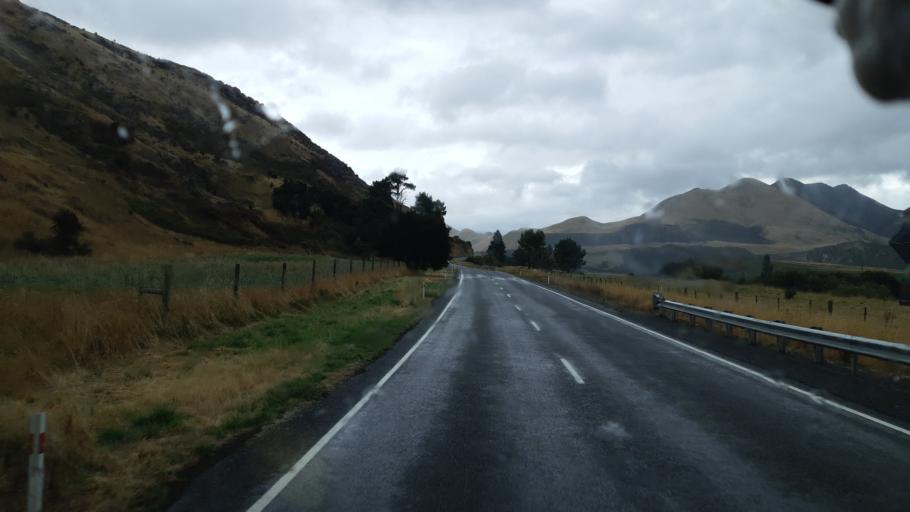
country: NZ
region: Canterbury
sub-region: Hurunui District
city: Amberley
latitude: -42.6356
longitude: 172.7723
